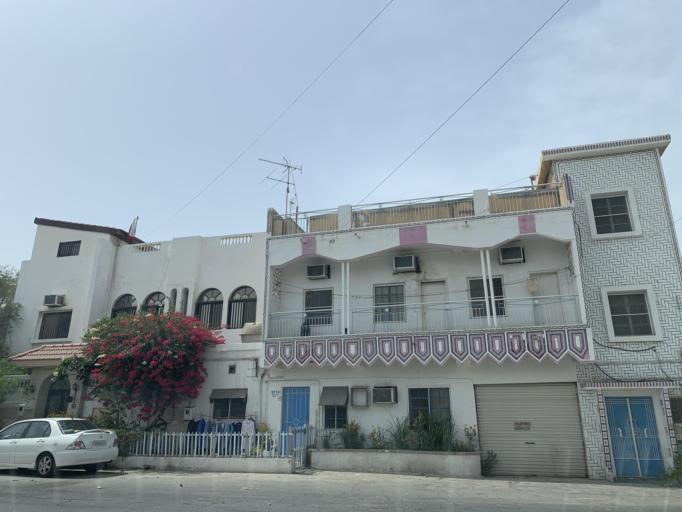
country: BH
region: Northern
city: Ar Rifa'
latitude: 26.1297
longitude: 50.5562
